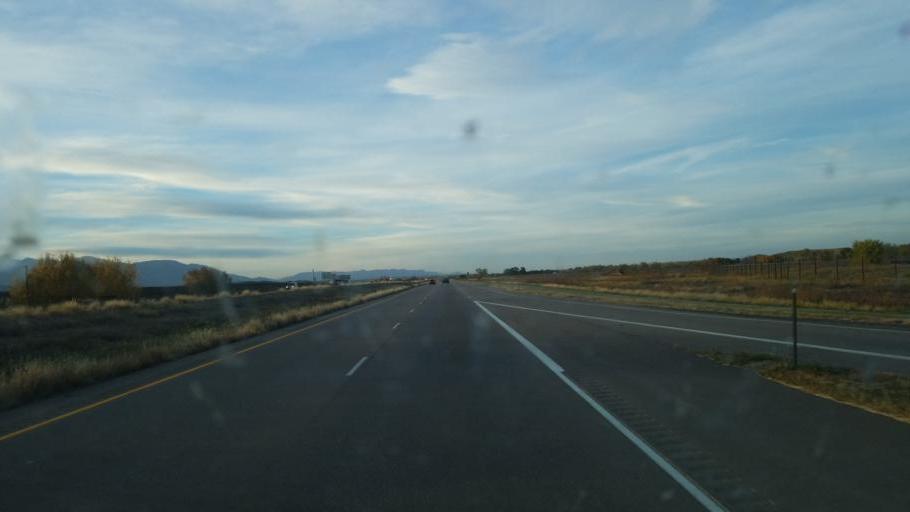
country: US
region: Colorado
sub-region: El Paso County
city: Fountain
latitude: 38.5892
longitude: -104.6705
